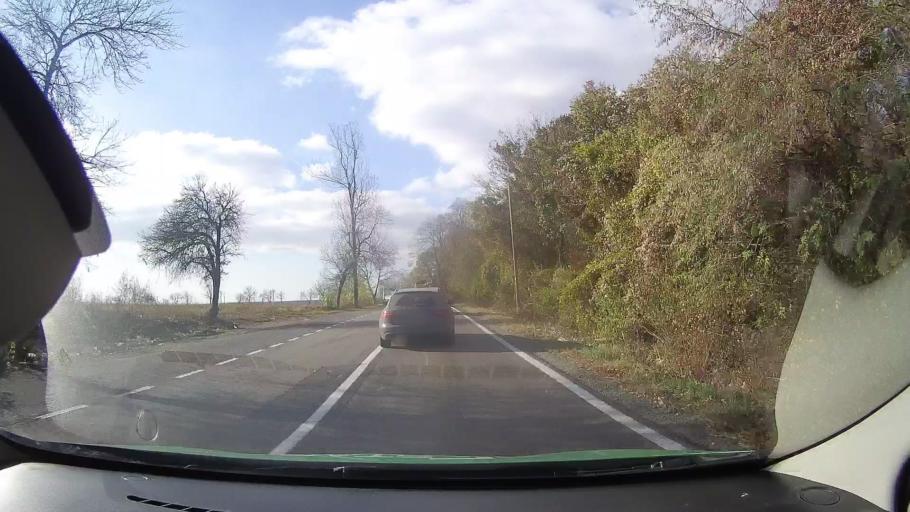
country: RO
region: Tulcea
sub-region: Comuna Topolog
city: Topolog
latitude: 44.9073
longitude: 28.4093
